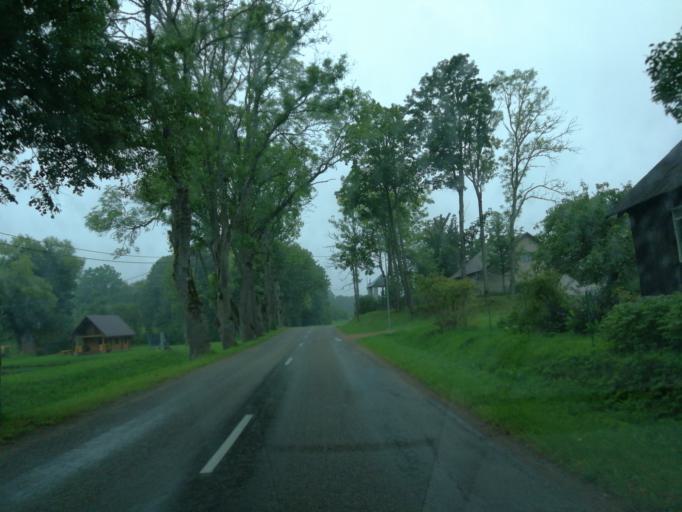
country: LV
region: Preilu Rajons
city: Jaunaglona
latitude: 56.2698
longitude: 27.0385
